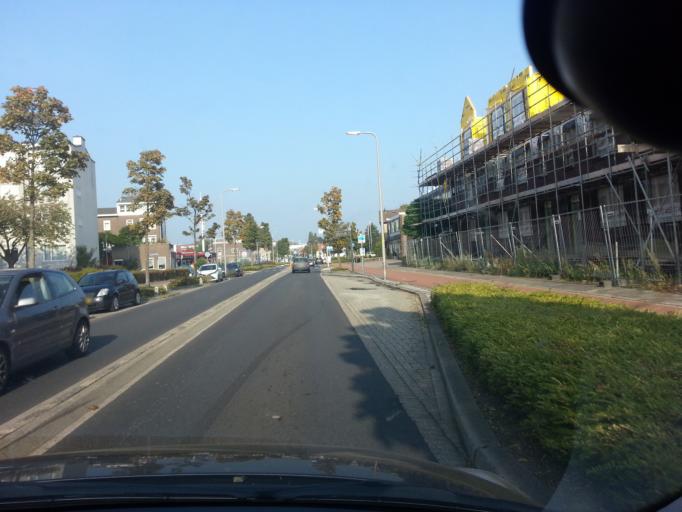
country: NL
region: South Holland
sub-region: Gemeente Zwijndrecht
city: Zwijndrecht
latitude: 51.8183
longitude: 4.6430
